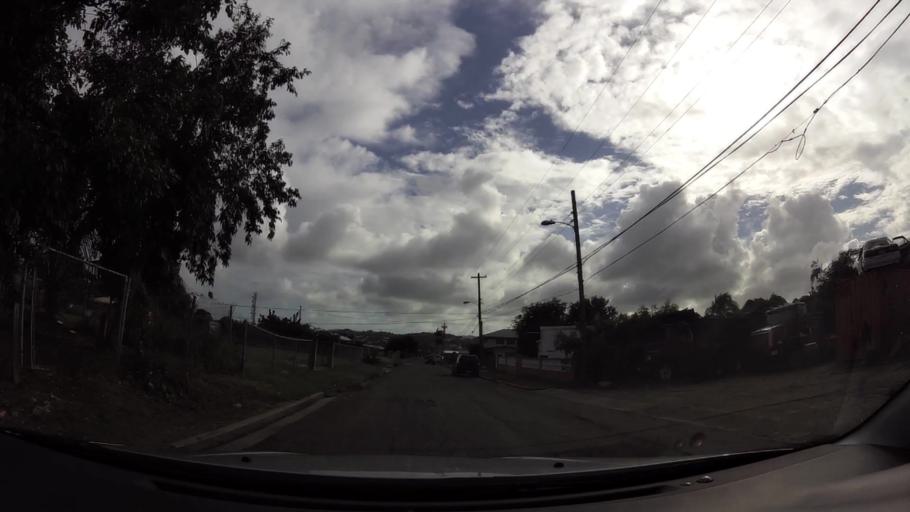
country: AG
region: Saint George
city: Piggotts
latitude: 17.1307
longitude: -61.8225
